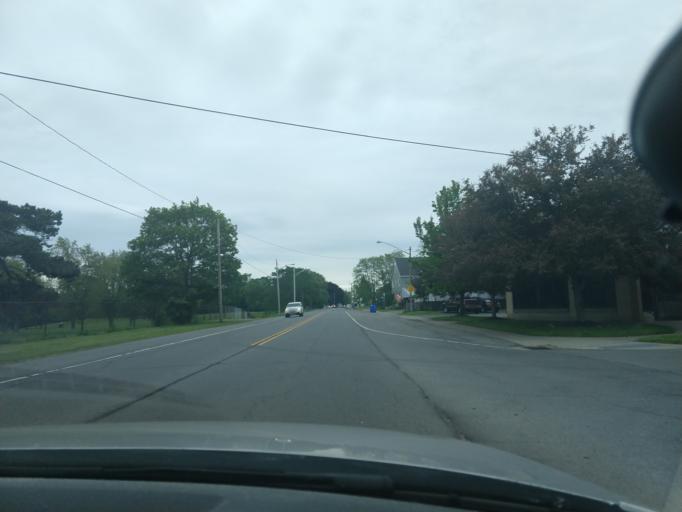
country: US
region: New York
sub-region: Erie County
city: West Seneca
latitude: 42.8391
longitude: -78.7997
